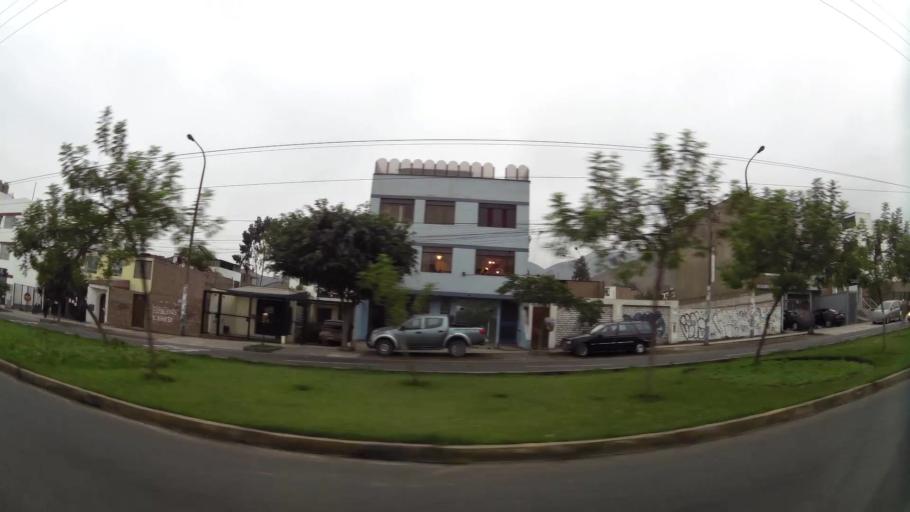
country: PE
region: Lima
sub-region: Lima
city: La Molina
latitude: -12.1046
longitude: -76.9413
